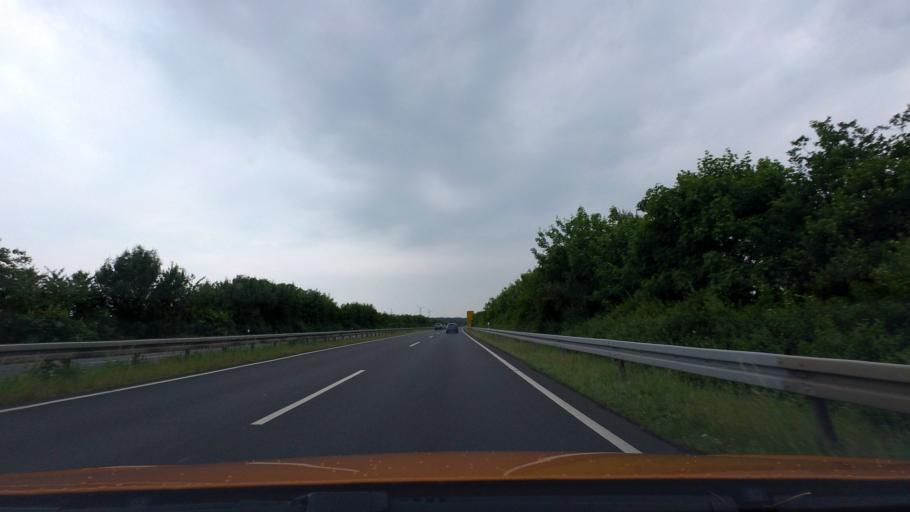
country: DE
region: Lower Saxony
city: Marklohe
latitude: 52.6530
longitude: 9.1626
